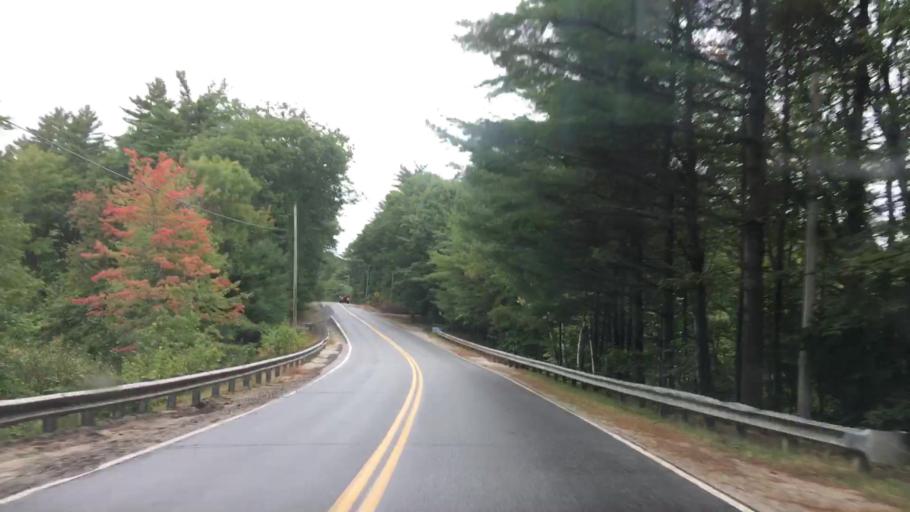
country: US
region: Maine
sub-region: Cumberland County
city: Raymond
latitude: 43.9495
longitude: -70.4628
